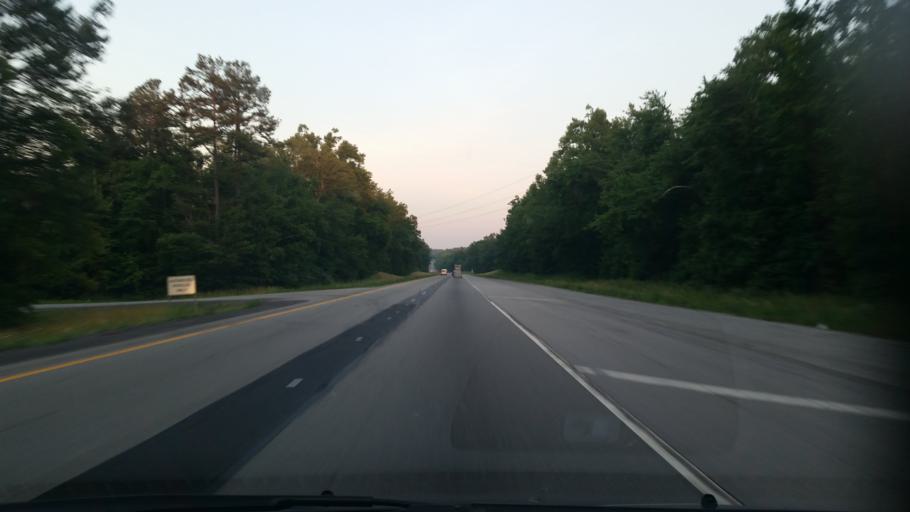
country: US
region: Tennessee
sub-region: Putnam County
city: Monterey
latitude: 36.0781
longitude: -85.2075
